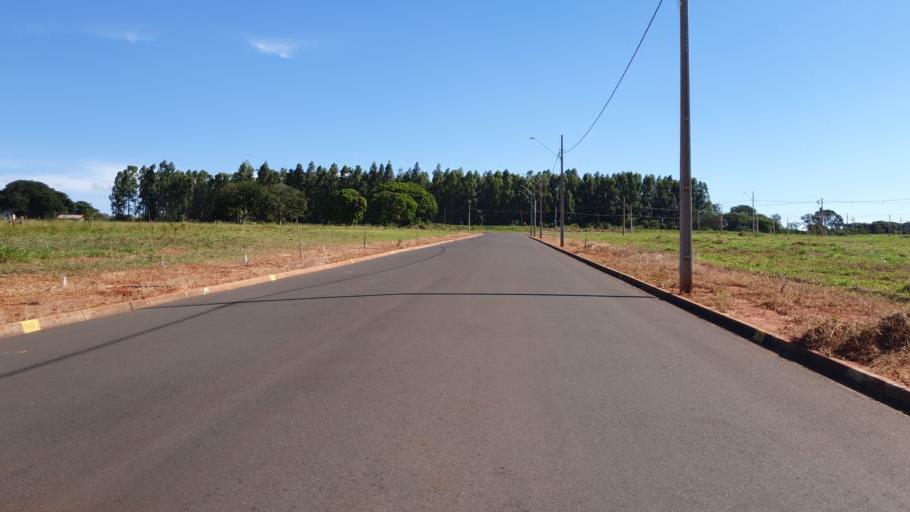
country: BR
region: Sao Paulo
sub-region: Paraguacu Paulista
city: Paraguacu Paulista
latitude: -22.3994
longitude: -50.5767
